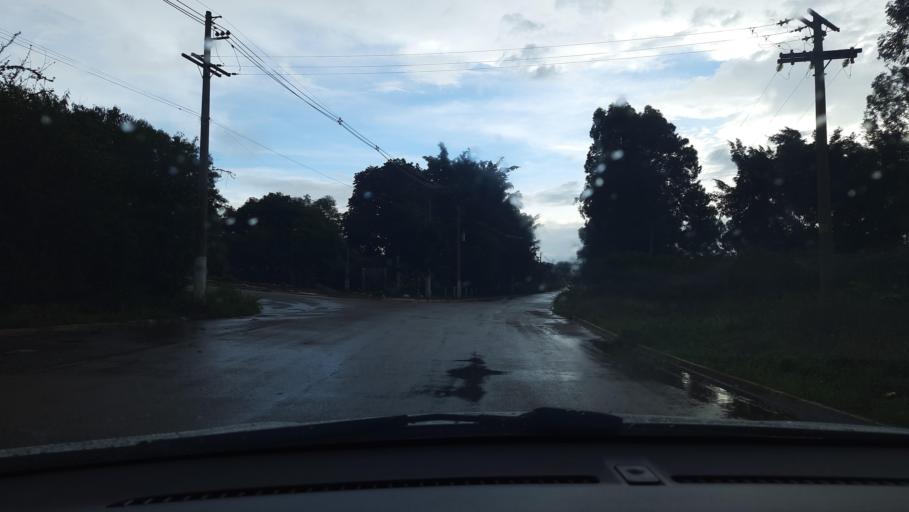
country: BR
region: Sao Paulo
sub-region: Casa Branca
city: Casa Branca
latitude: -21.7506
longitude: -47.0730
